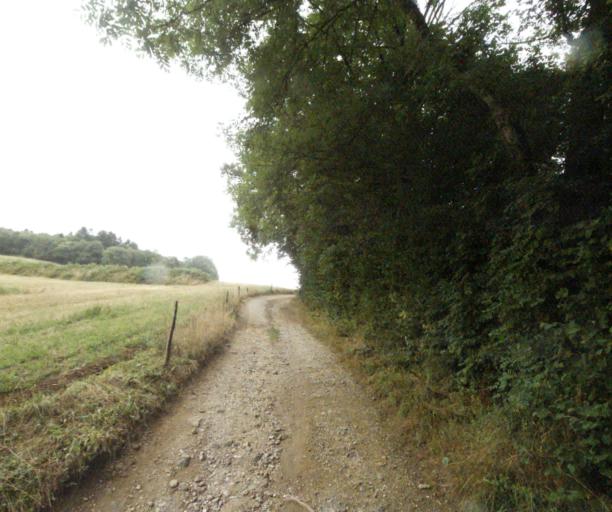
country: FR
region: Midi-Pyrenees
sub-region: Departement du Tarn
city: Soreze
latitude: 43.4149
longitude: 2.0718
